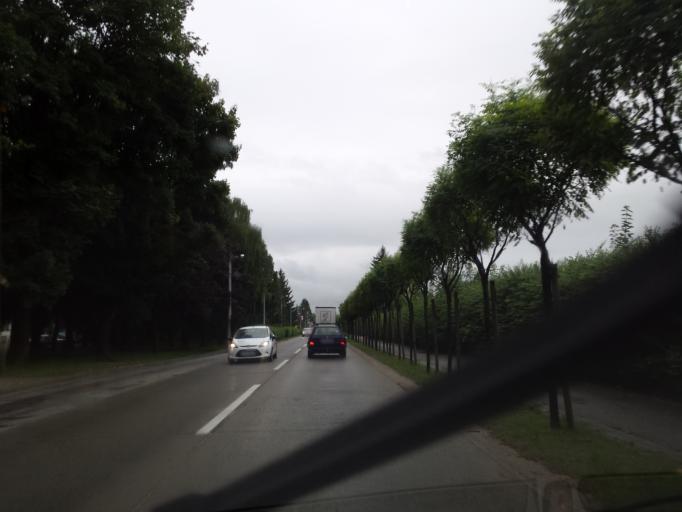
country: HR
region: Zagrebacka
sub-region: Grad Samobor
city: Samobor
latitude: 45.8020
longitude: 15.7230
